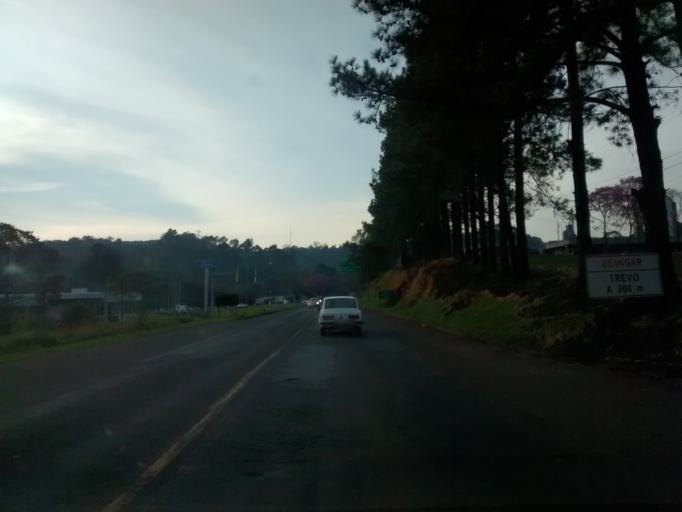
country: BR
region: Parana
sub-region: Francisco Beltrao
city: Francisco Beltrao
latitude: -26.1139
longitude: -53.0442
